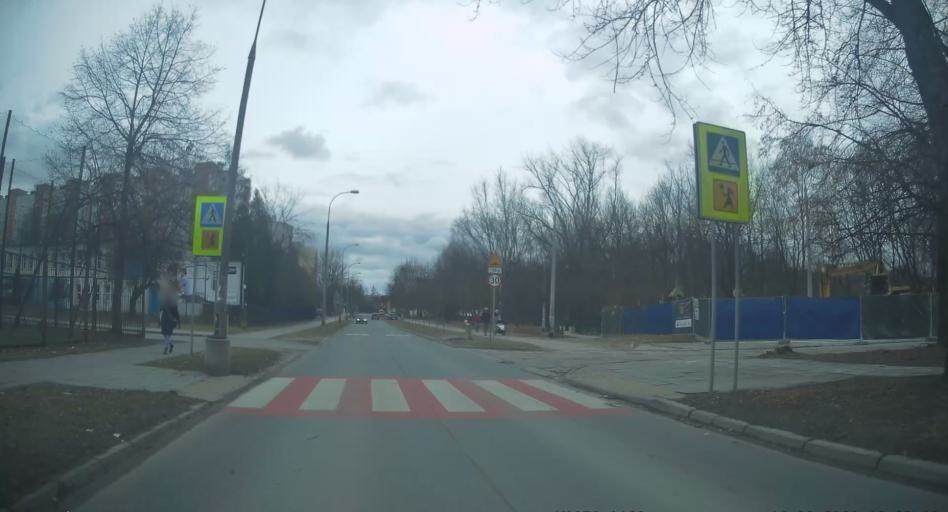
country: PL
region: Lesser Poland Voivodeship
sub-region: Powiat wielicki
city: Czarnochowice
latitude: 50.0120
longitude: 20.0163
